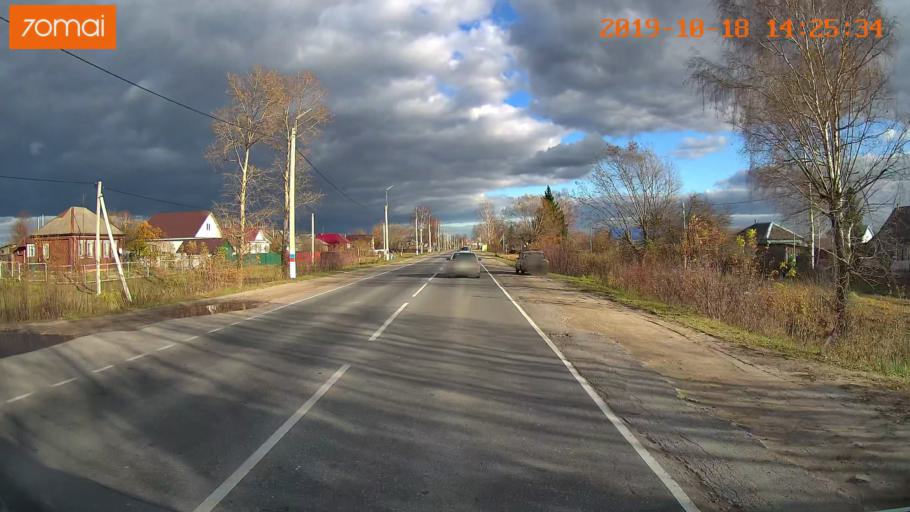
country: RU
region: Rjazan
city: Tuma
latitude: 55.1467
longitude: 40.5194
